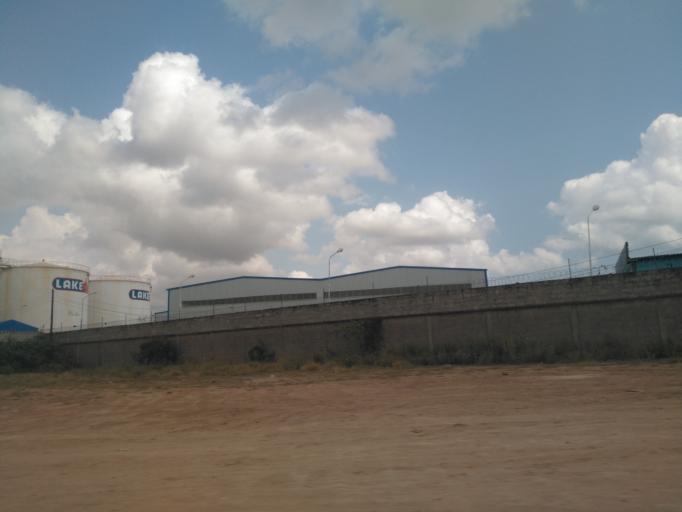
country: TZ
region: Dar es Salaam
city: Dar es Salaam
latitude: -6.8473
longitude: 39.3155
